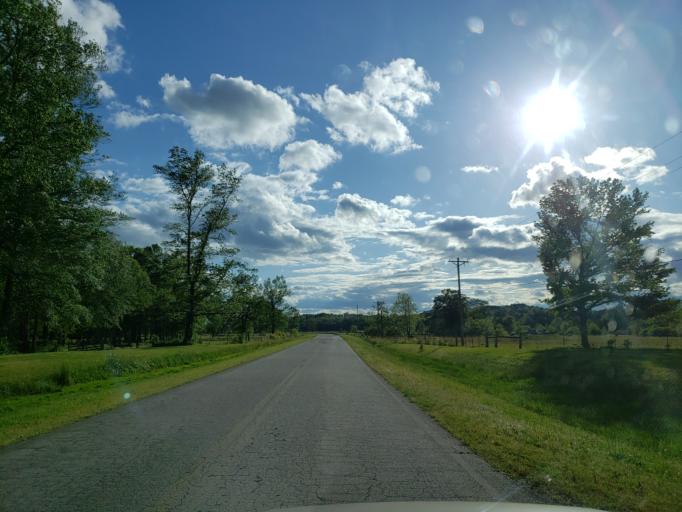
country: US
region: Georgia
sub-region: Haralson County
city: Tallapoosa
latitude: 33.7866
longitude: -85.2991
